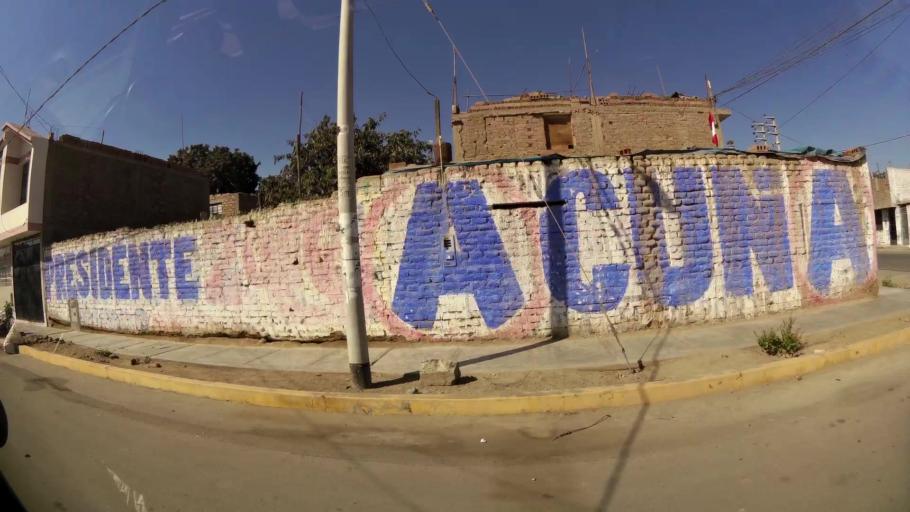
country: PE
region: Ica
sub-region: Provincia de Ica
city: La Tinguina
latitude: -14.0361
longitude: -75.7064
